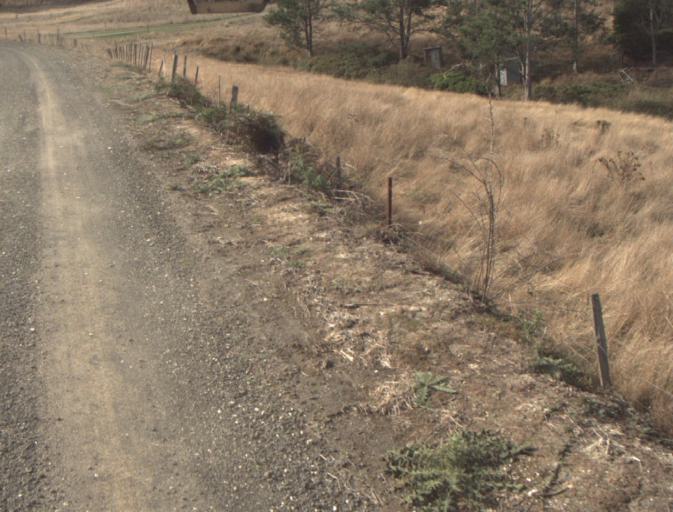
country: AU
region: Tasmania
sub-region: Launceston
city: Mayfield
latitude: -41.1961
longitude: 147.1950
